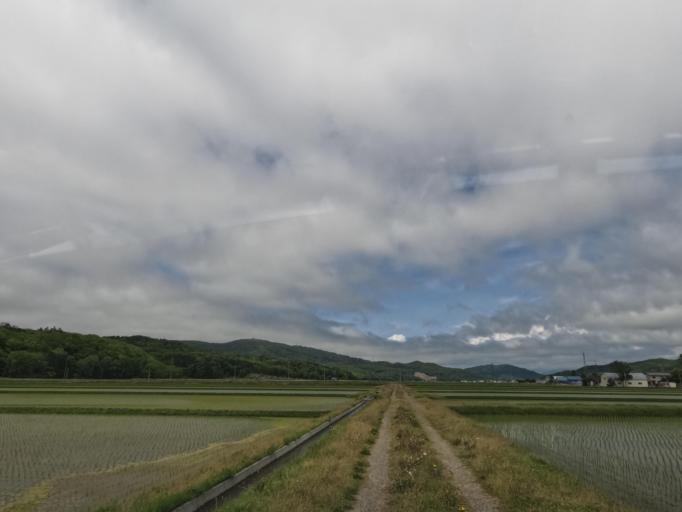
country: JP
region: Hokkaido
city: Tobetsu
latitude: 43.2676
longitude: 141.5267
